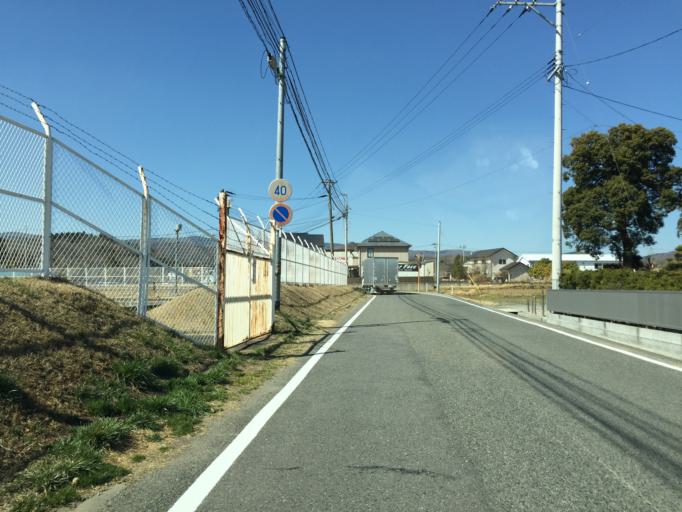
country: JP
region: Fukushima
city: Iwaki
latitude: 37.0608
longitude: 140.8483
